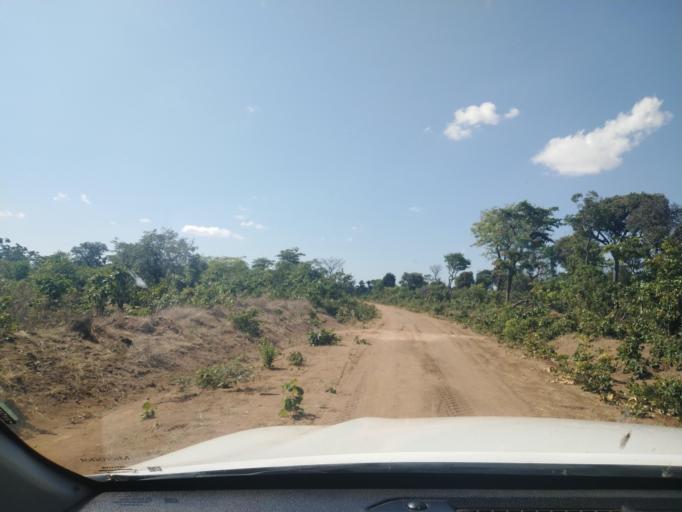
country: ZM
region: Northern
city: Chinsali
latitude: -11.0059
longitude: 31.7741
